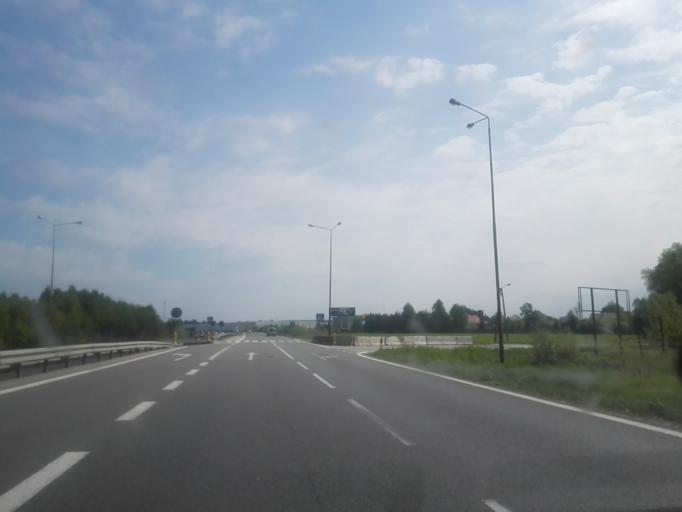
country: PL
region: Lodz Voivodeship
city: Zabia Wola
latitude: 52.0346
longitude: 20.6893
